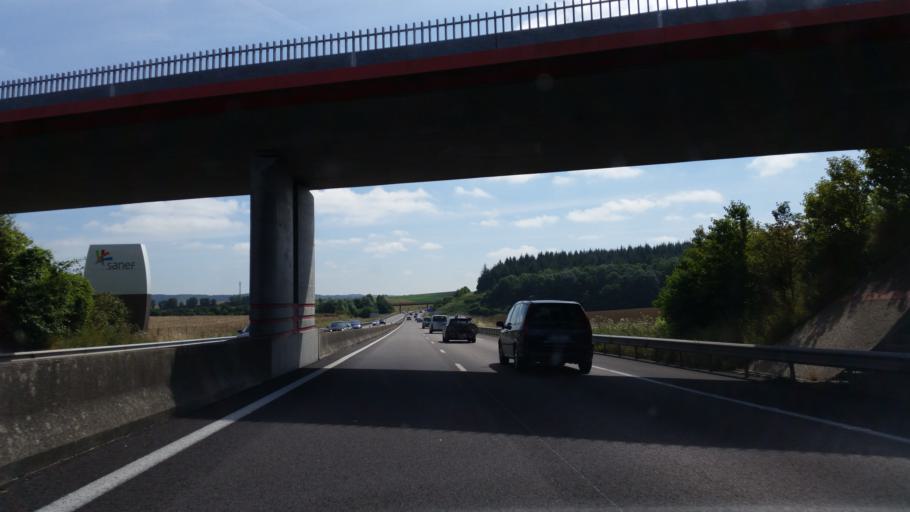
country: FR
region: Haute-Normandie
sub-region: Departement de la Seine-Maritime
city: Neufchatel-en-Bray
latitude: 49.7561
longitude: 1.4925
